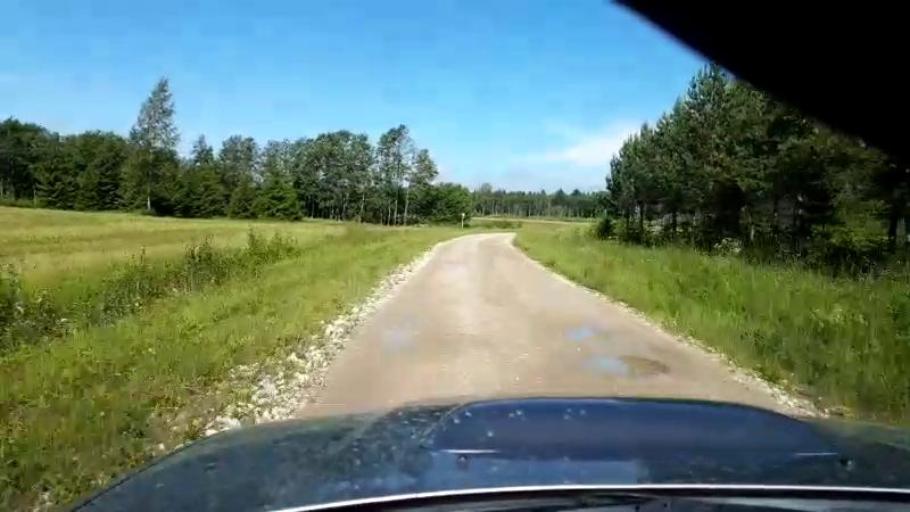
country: EE
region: Paernumaa
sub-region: Sindi linn
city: Sindi
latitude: 58.5105
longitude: 24.6876
